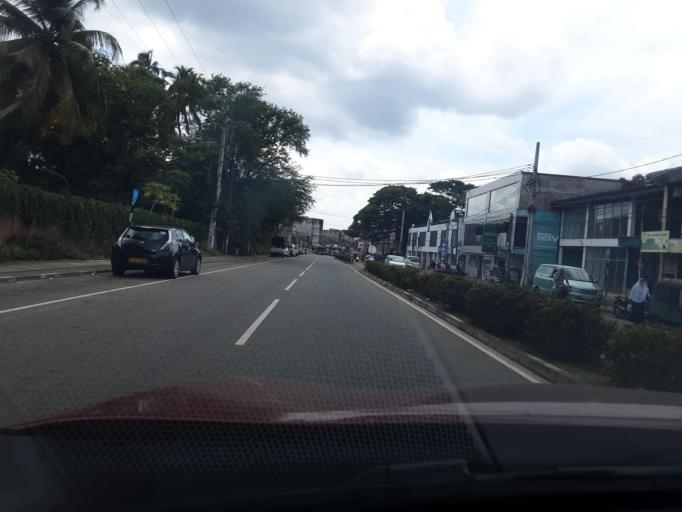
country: LK
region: North Western
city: Kurunegala
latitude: 7.4324
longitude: 80.2131
